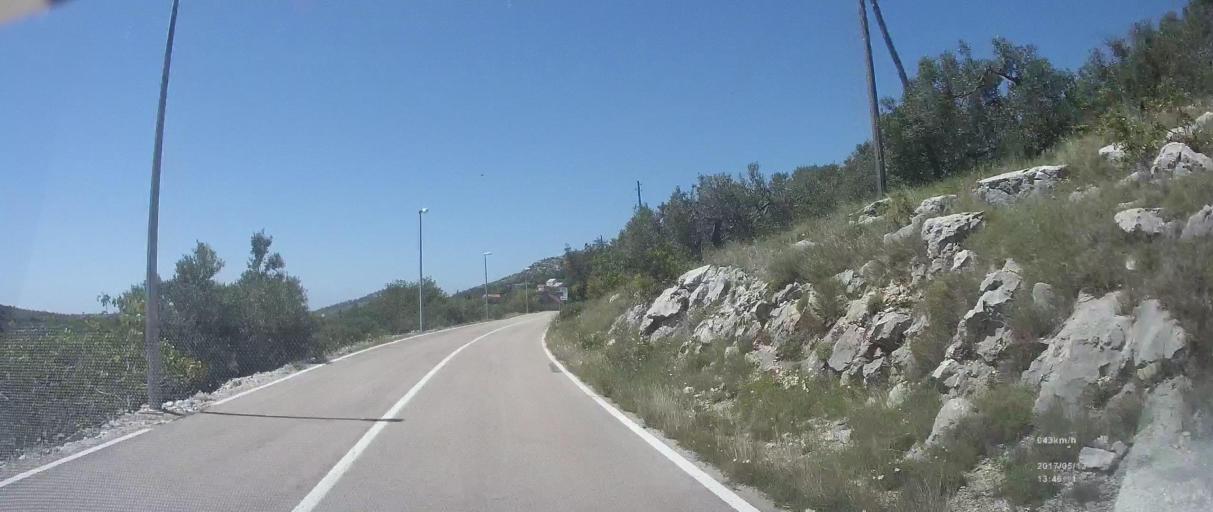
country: HR
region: Sibensko-Kniniska
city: Primosten
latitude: 43.6096
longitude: 15.9850
